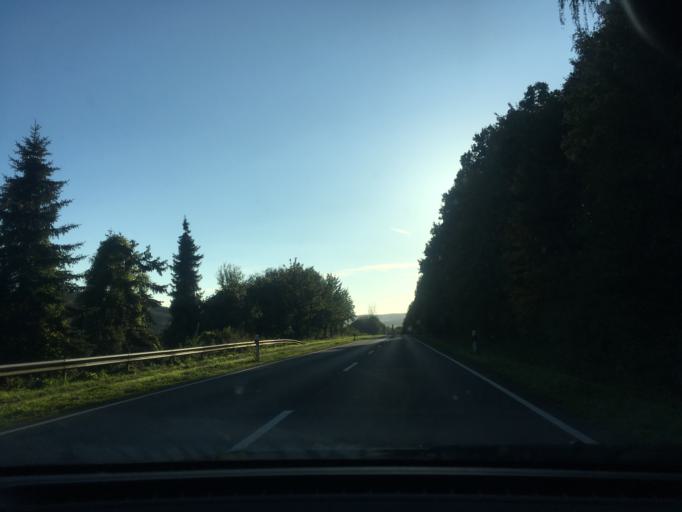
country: DE
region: Lower Saxony
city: Dassel
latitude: 51.8031
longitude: 9.7136
